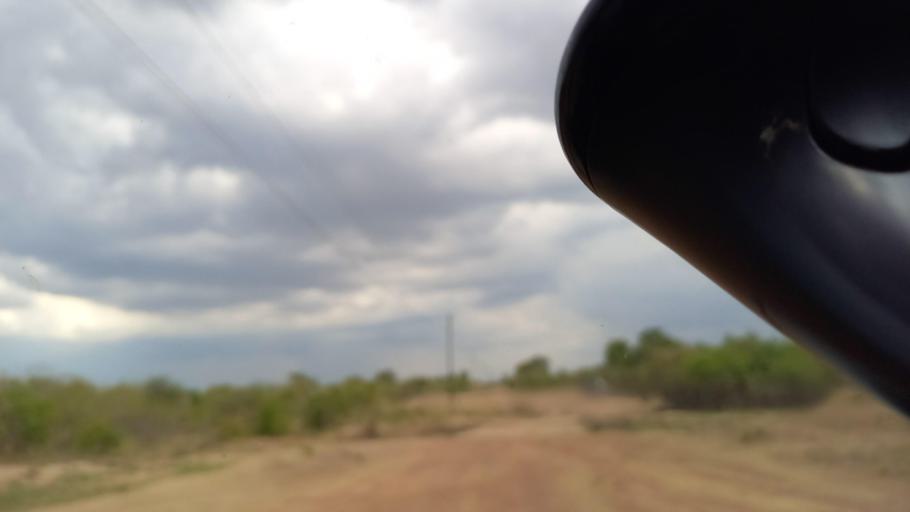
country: ZM
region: Lusaka
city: Kafue
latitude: -15.8503
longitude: 28.1102
